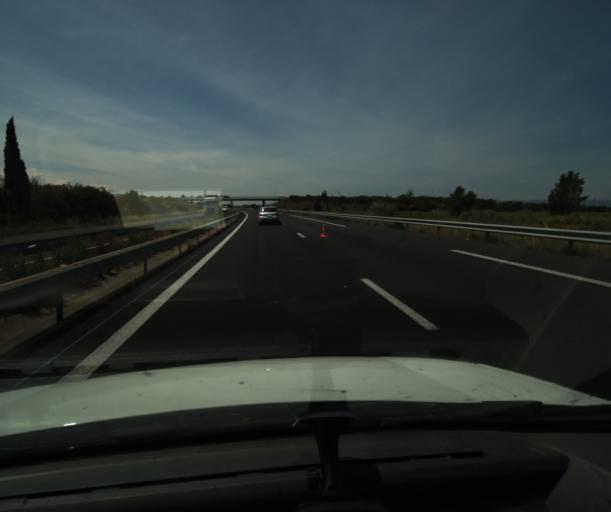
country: FR
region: Languedoc-Roussillon
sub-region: Departement de l'Aude
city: Ornaisons
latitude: 43.1667
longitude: 2.8338
